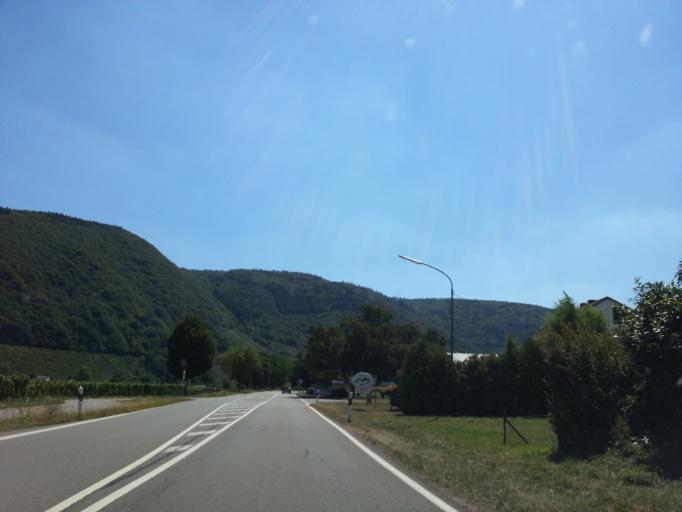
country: DE
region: Rheinland-Pfalz
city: Polich
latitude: 49.8006
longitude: 6.8487
